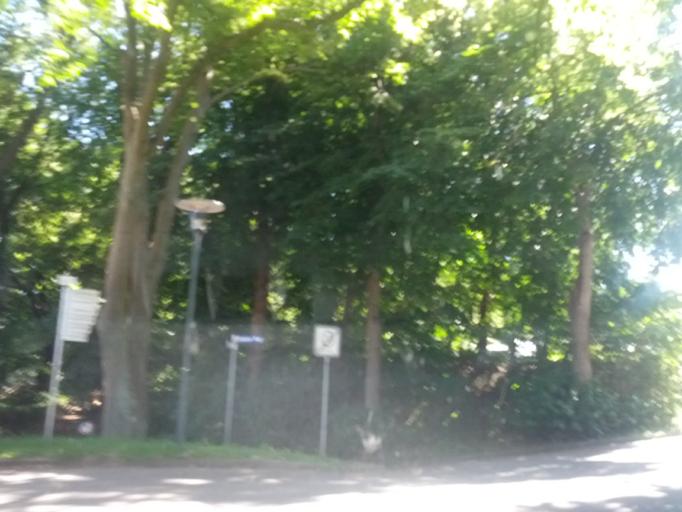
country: DE
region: Mecklenburg-Vorpommern
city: Bergen auf Ruegen
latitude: 54.4222
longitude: 13.4402
